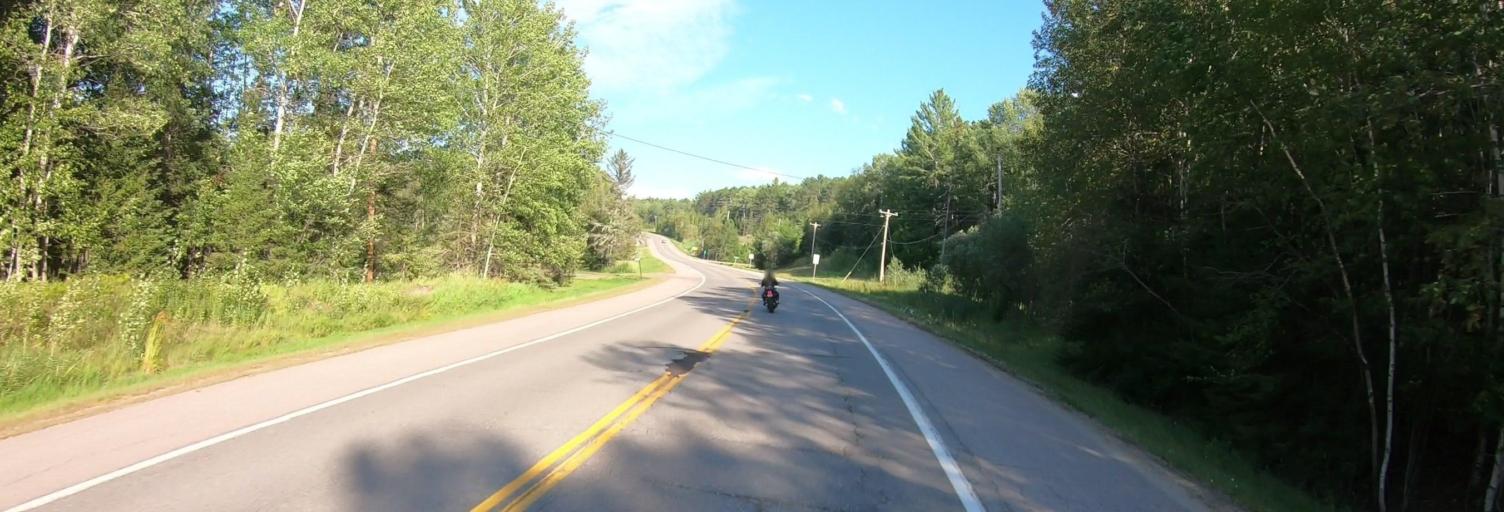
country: US
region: Minnesota
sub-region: Saint Louis County
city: Ely
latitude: 47.9254
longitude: -91.7882
